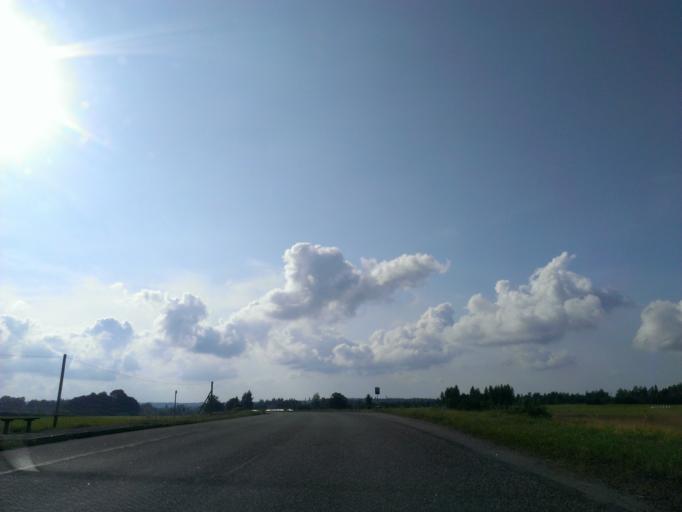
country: LV
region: Priekuli
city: Priekuli
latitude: 57.2993
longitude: 25.4141
